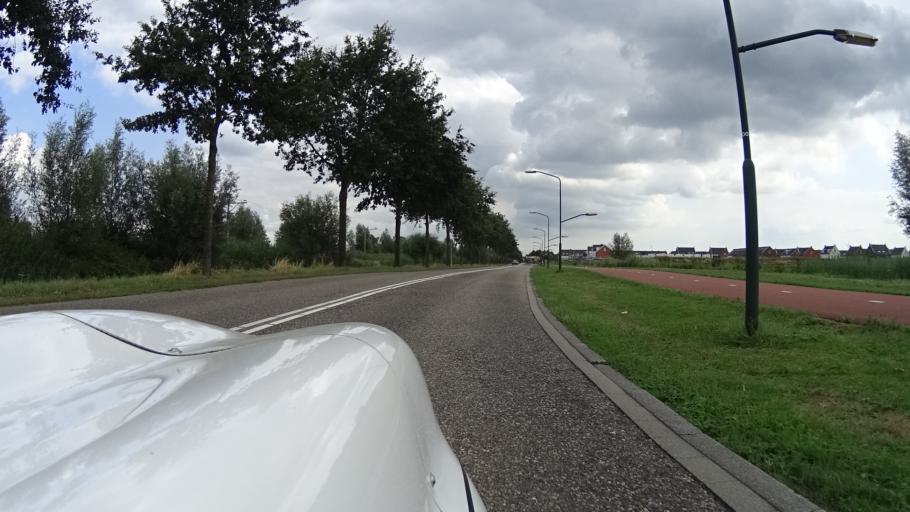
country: NL
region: South Holland
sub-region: Gemeente Sliedrecht
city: Sliedrecht
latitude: 51.8290
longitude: 4.8078
